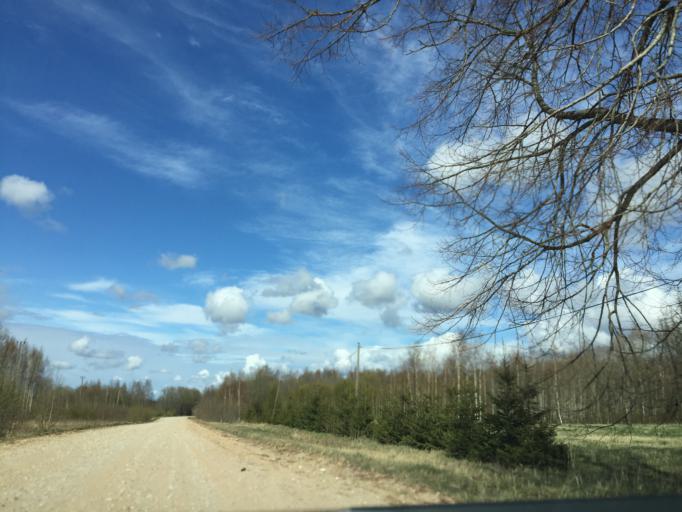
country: LV
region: Limbazu Rajons
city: Limbazi
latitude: 57.5762
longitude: 24.5947
